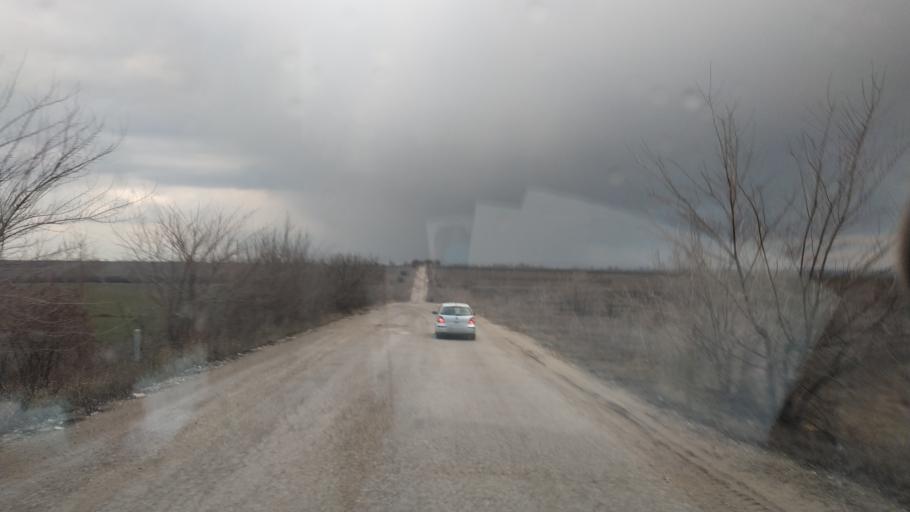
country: MD
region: Telenesti
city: Grigoriopol
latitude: 47.0587
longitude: 29.2959
